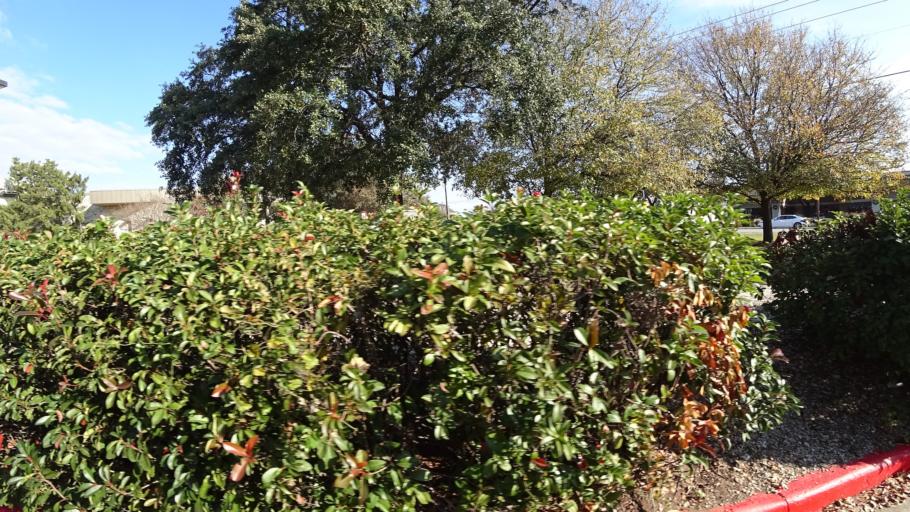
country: US
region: Texas
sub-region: Williamson County
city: Jollyville
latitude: 30.3951
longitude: -97.7502
